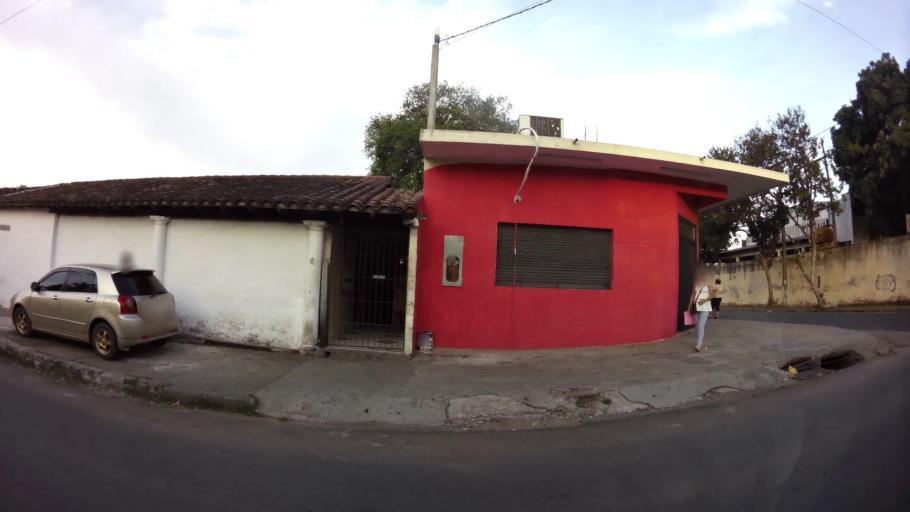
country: PY
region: Central
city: San Lorenzo
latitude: -25.3410
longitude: -57.5023
